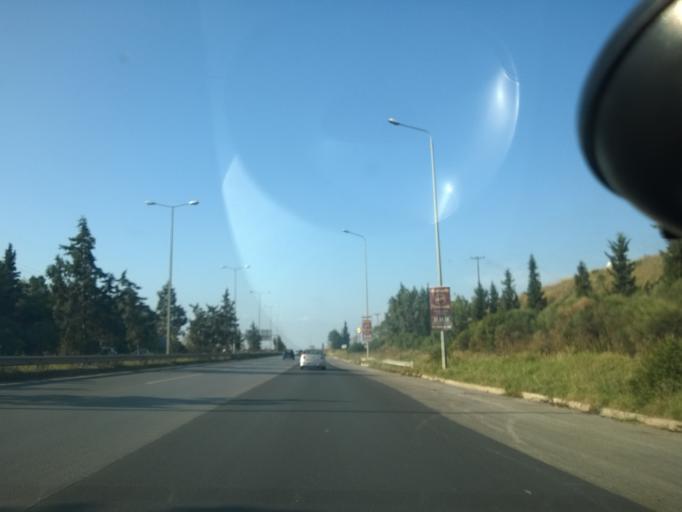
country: GR
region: Central Macedonia
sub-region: Nomos Thessalonikis
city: Pylaia
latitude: 40.5849
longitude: 22.9738
